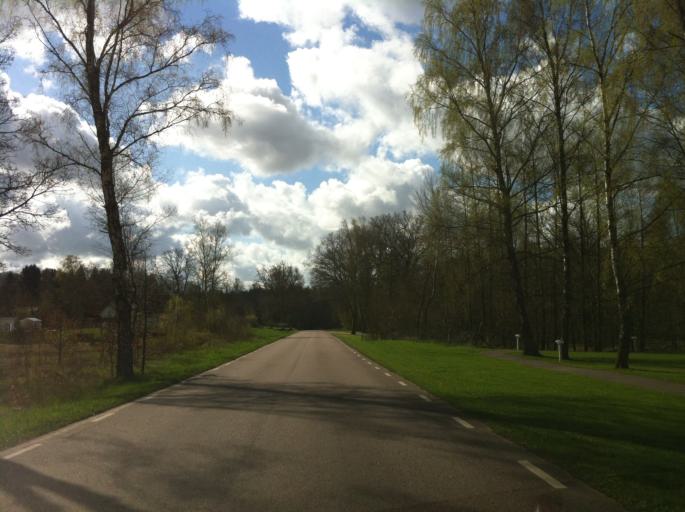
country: SE
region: Skane
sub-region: Hoors Kommun
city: Satofta
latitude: 55.8970
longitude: 13.6114
